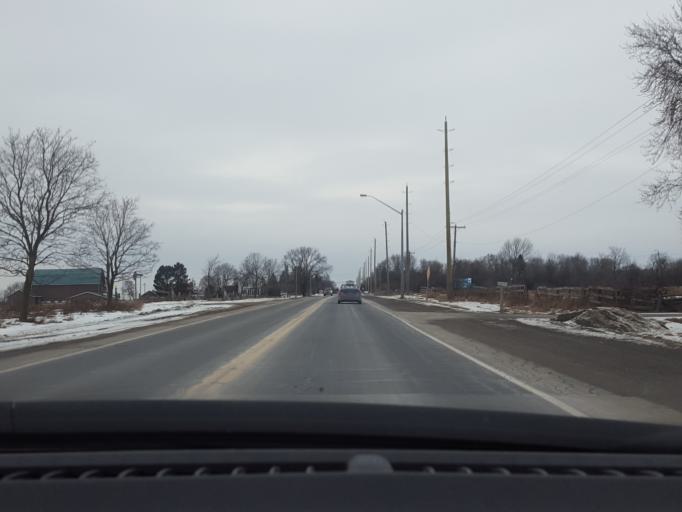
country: CA
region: Ontario
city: Keswick
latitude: 44.1615
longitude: -79.4304
